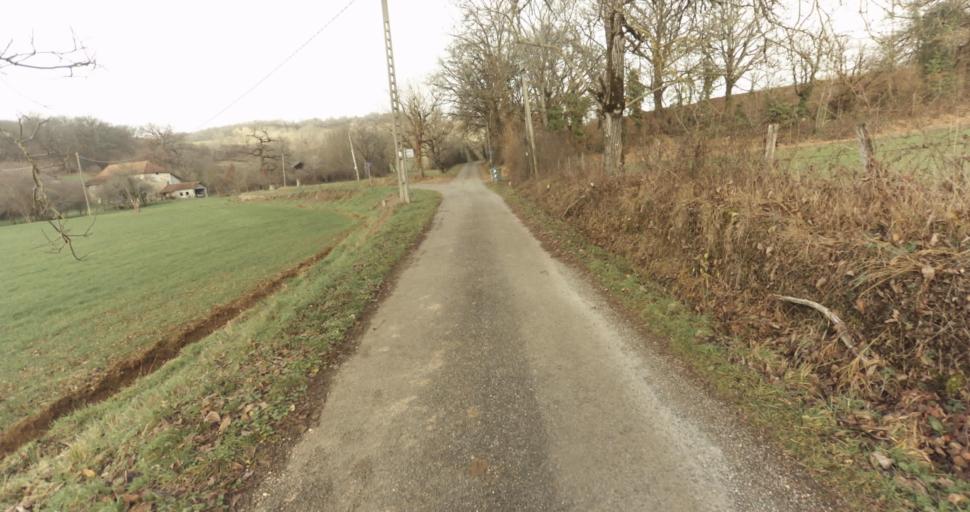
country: FR
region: Midi-Pyrenees
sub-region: Departement du Lot
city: Figeac
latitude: 44.6184
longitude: 2.0155
